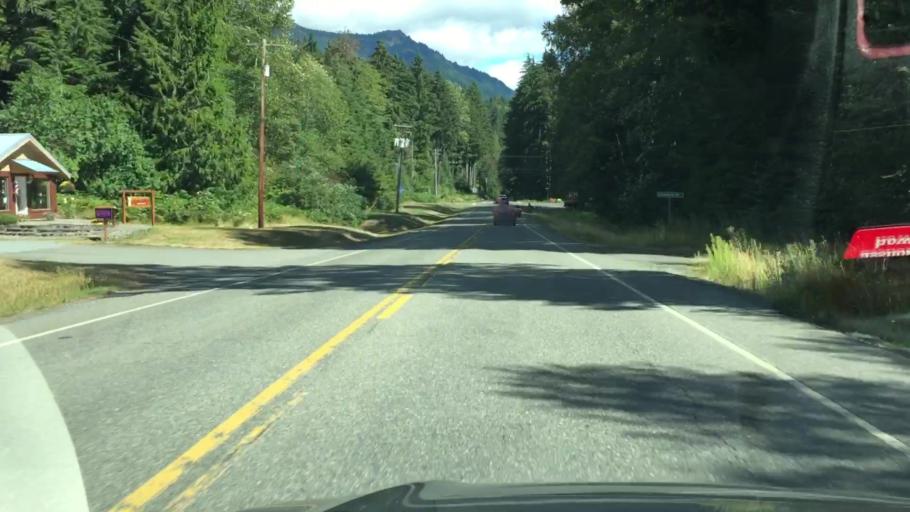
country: US
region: Washington
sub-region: Pierce County
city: Eatonville
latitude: 46.7573
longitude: -121.9841
